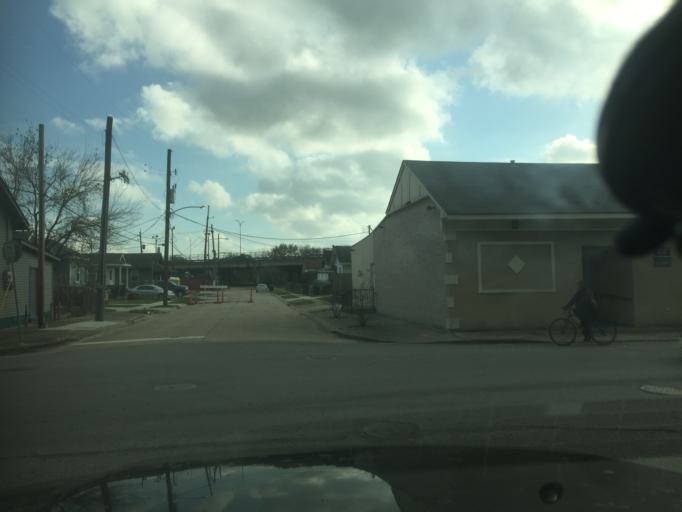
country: US
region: Louisiana
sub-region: Orleans Parish
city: New Orleans
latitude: 29.9939
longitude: -90.0758
